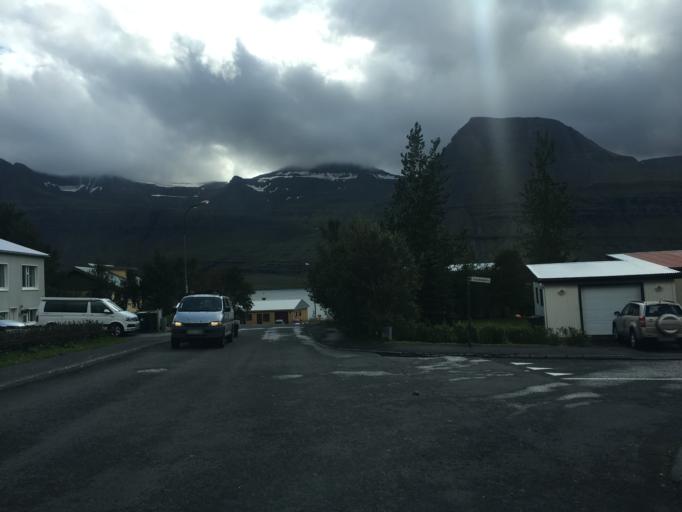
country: IS
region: East
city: Reydarfjoerdur
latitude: 65.0335
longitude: -14.2140
